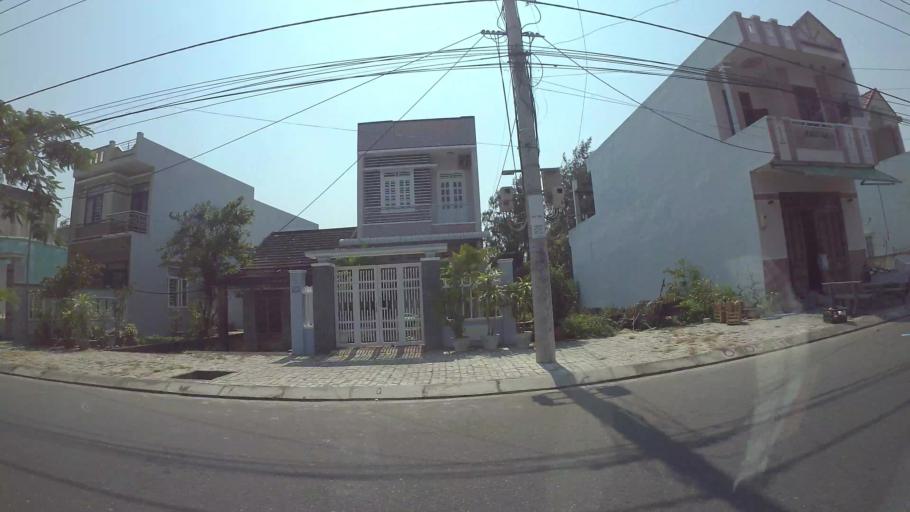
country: VN
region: Da Nang
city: Ngu Hanh Son
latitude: 15.9882
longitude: 108.2685
